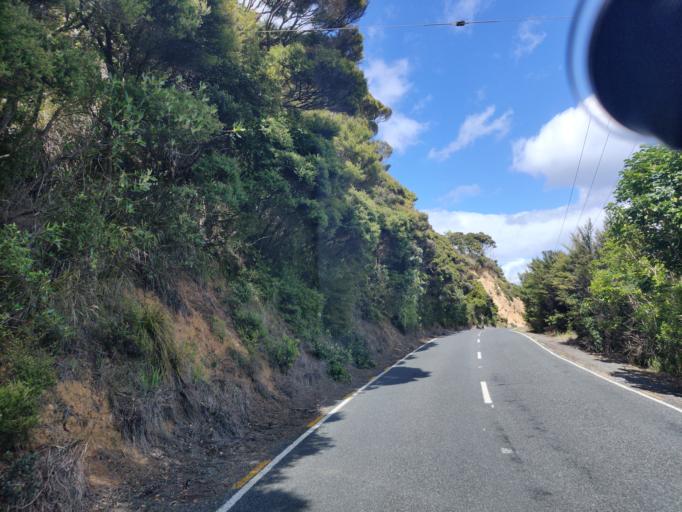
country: NZ
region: Northland
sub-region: Far North District
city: Paihia
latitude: -35.2584
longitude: 174.2333
